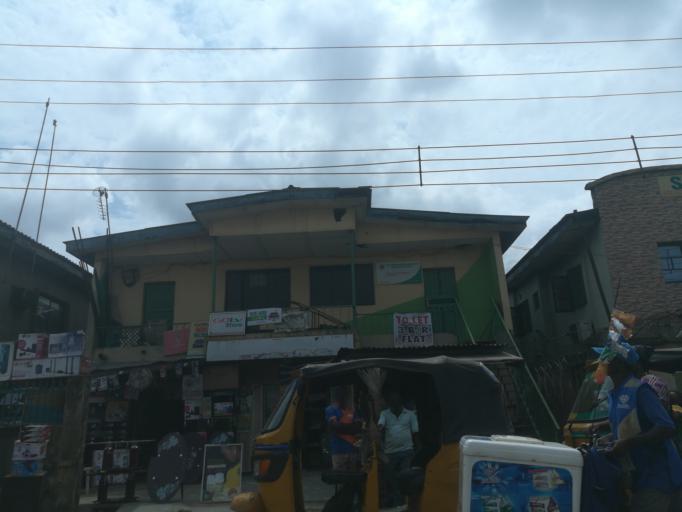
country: NG
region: Lagos
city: Somolu
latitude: 6.5410
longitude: 3.3929
